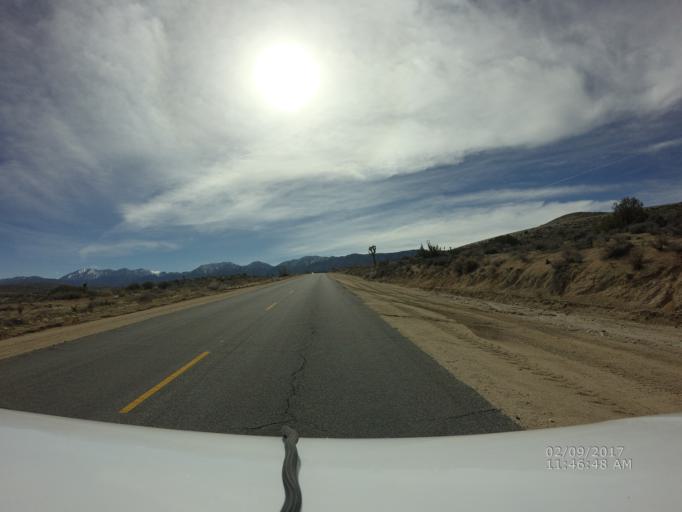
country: US
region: California
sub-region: Los Angeles County
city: Littlerock
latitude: 34.4930
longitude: -117.9142
